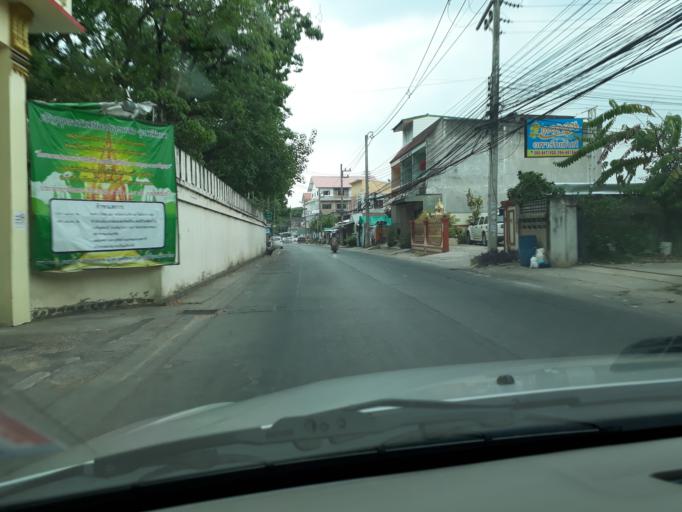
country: TH
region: Khon Kaen
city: Khon Kaen
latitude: 16.4187
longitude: 102.8425
